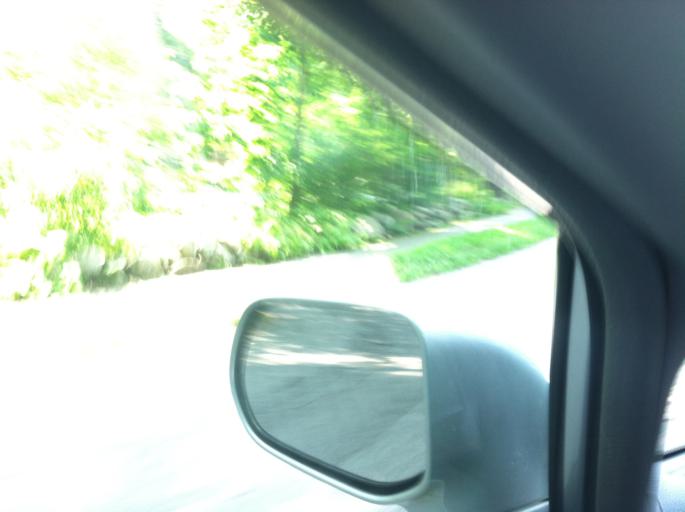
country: US
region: Massachusetts
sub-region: Middlesex County
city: Bedford
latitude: 42.5063
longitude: -71.2822
